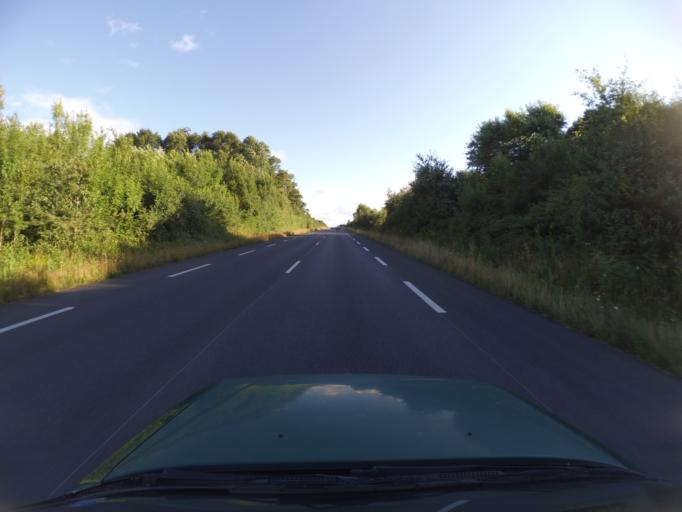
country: FR
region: Pays de la Loire
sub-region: Departement de la Vendee
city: Saint-Hilaire-de-Loulay
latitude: 46.9897
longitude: -1.3521
